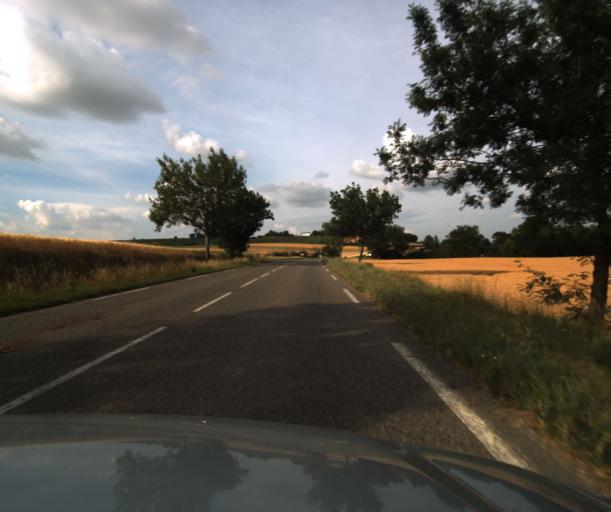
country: FR
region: Midi-Pyrenees
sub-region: Departement du Tarn-et-Garonne
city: Beaumont-de-Lomagne
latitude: 43.8694
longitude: 0.9626
